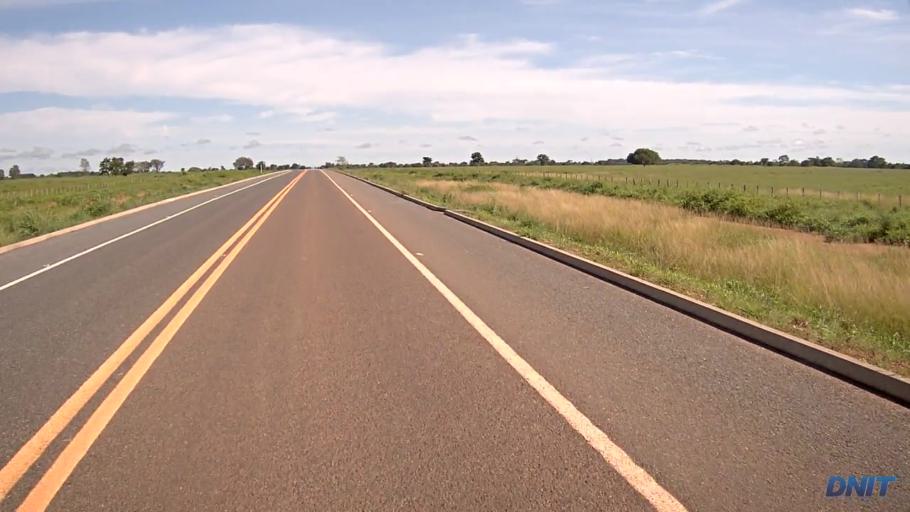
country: BR
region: Goias
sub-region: Sao Miguel Do Araguaia
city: Sao Miguel do Araguaia
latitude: -13.4870
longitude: -50.1101
